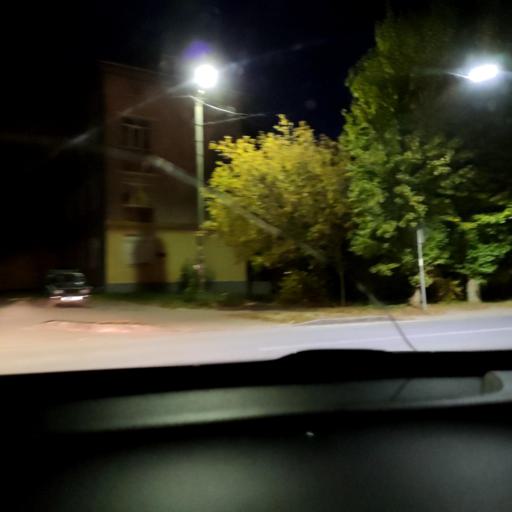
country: RU
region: Tatarstan
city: Vysokaya Gora
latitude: 55.8674
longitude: 49.2254
